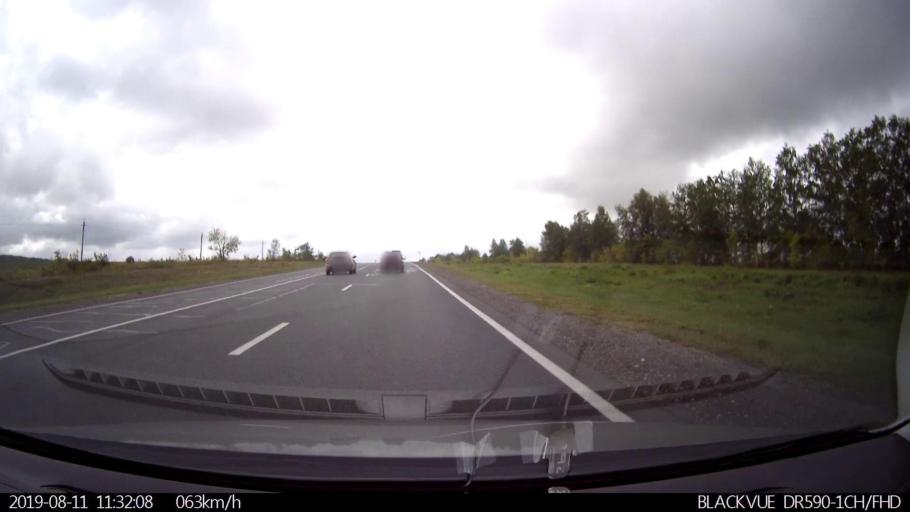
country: RU
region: Ulyanovsk
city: Krasnyy Gulyay
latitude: 54.0405
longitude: 48.2138
